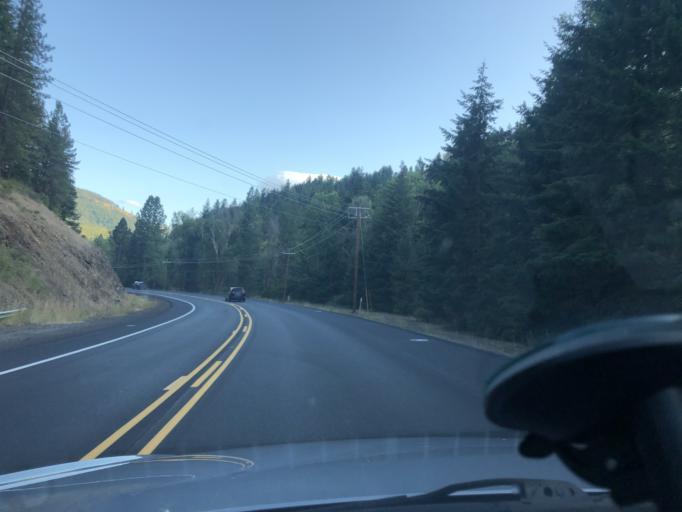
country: US
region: Washington
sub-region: Kittitas County
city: Cle Elum
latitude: 47.2157
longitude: -120.7007
